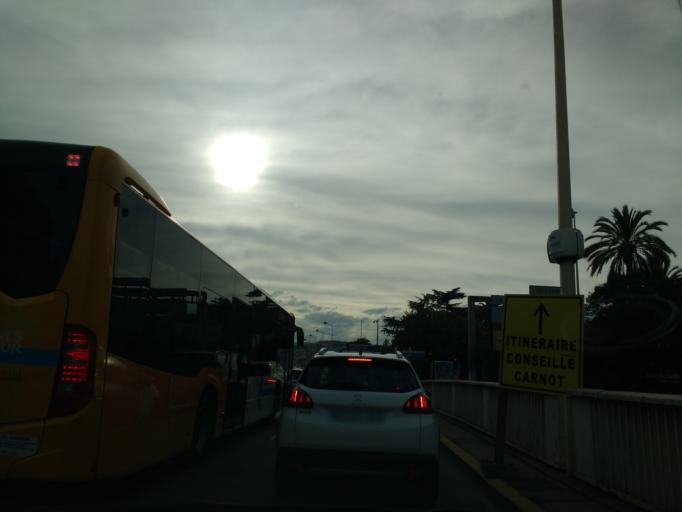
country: FR
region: Provence-Alpes-Cote d'Azur
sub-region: Departement des Alpes-Maritimes
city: Cannes
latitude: 43.5539
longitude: 7.0257
